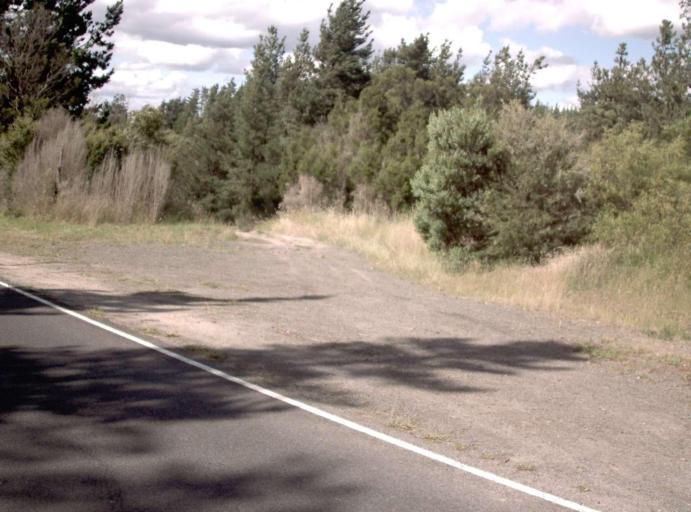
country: AU
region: Victoria
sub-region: Latrobe
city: Morwell
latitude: -38.1857
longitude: 146.4045
